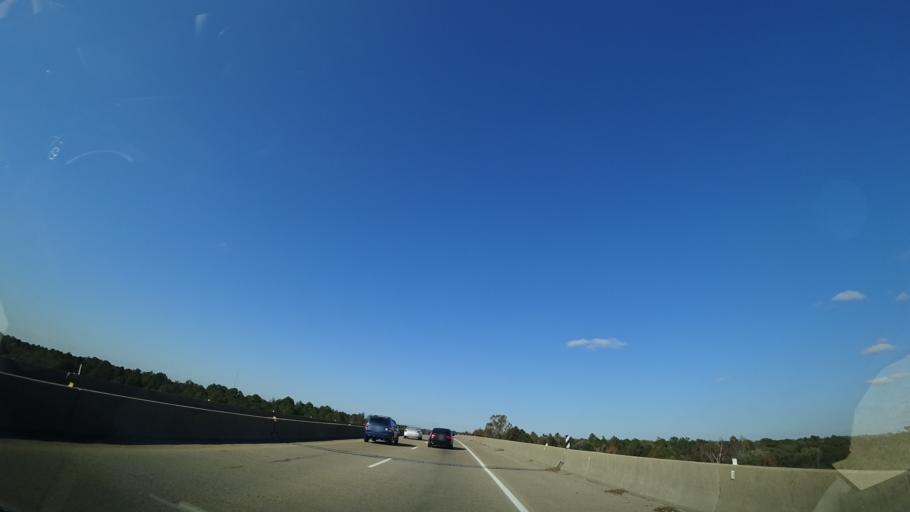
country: US
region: Virginia
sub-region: City of Chesapeake
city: Chesapeake
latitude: 36.7202
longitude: -76.2259
